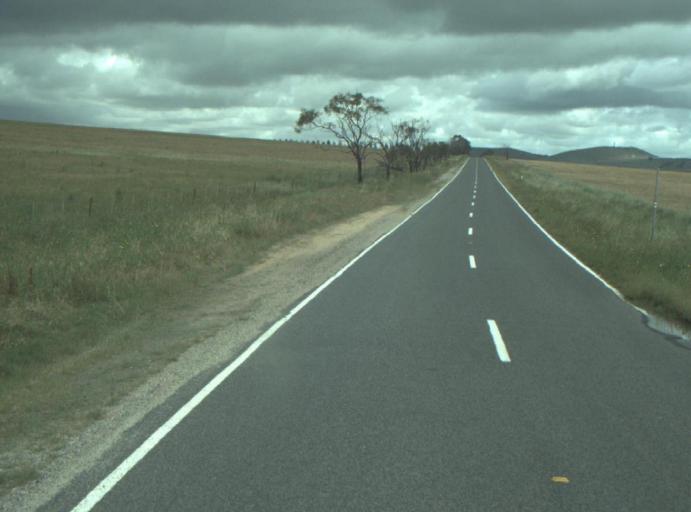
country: AU
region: Victoria
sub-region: Greater Geelong
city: Lara
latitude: -37.8928
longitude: 144.3664
